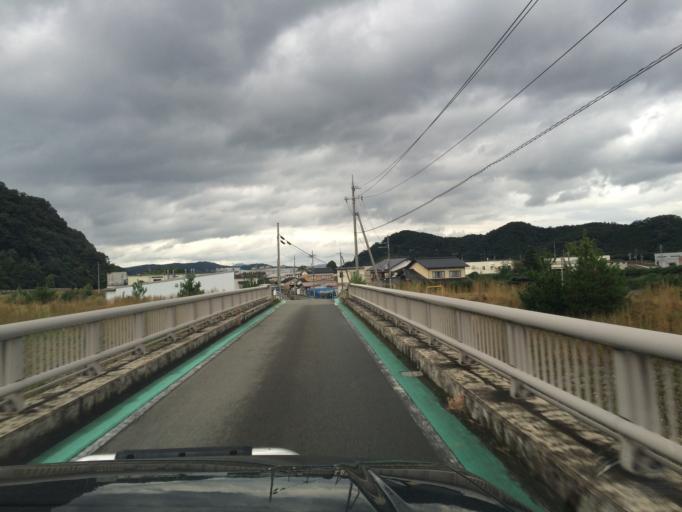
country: JP
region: Hyogo
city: Toyooka
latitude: 35.4575
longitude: 134.7696
